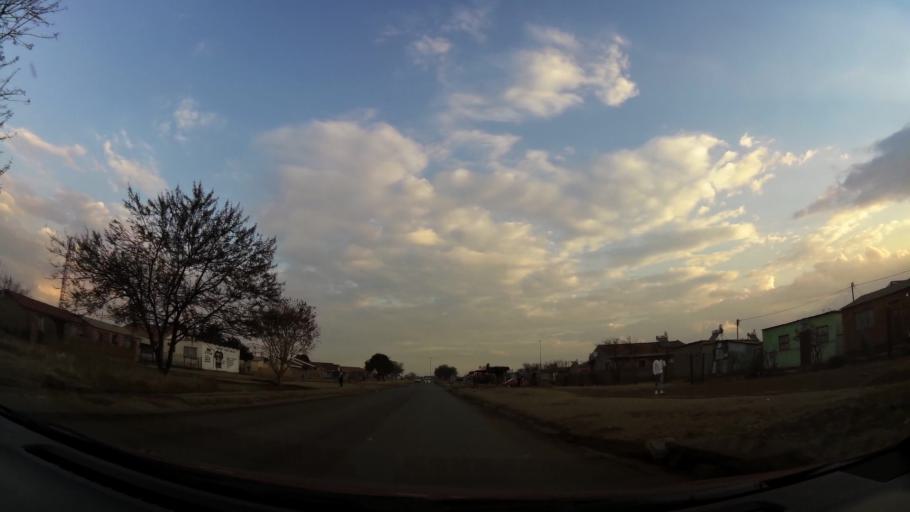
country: ZA
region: Gauteng
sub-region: City of Johannesburg Metropolitan Municipality
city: Orange Farm
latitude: -26.5588
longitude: 27.8385
